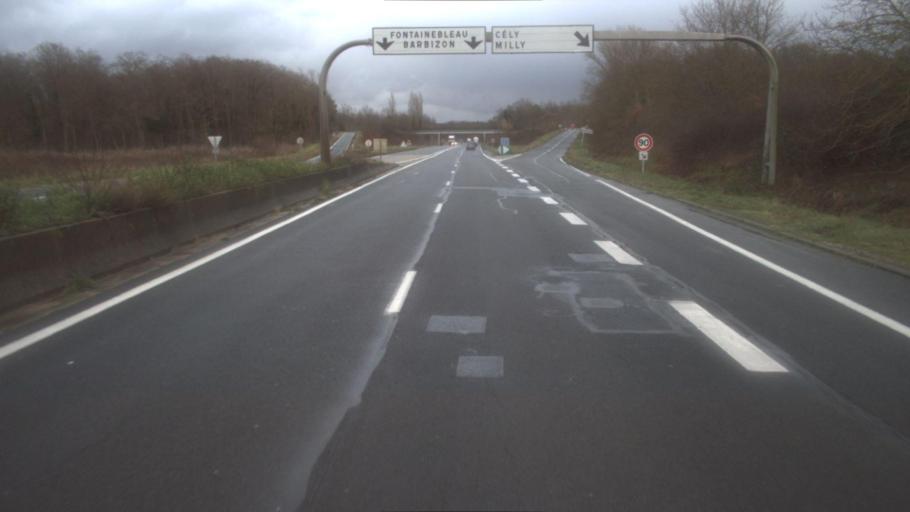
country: FR
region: Ile-de-France
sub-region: Departement de Seine-et-Marne
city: Cely
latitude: 48.4689
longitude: 2.5362
